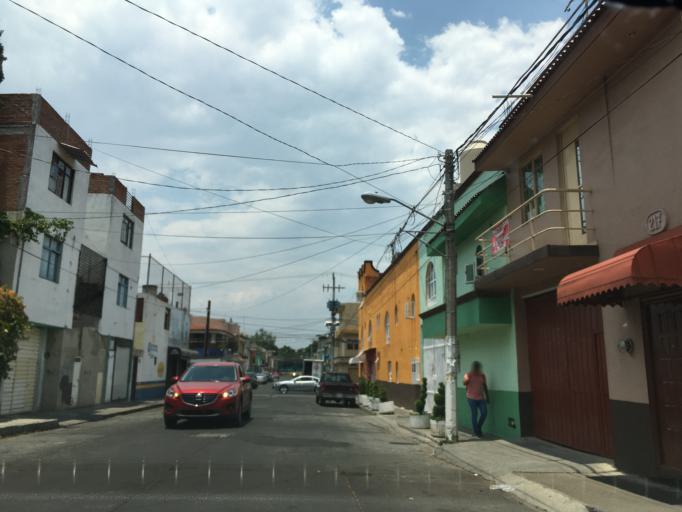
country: MX
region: Michoacan
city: Morelia
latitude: 19.6917
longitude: -101.2014
